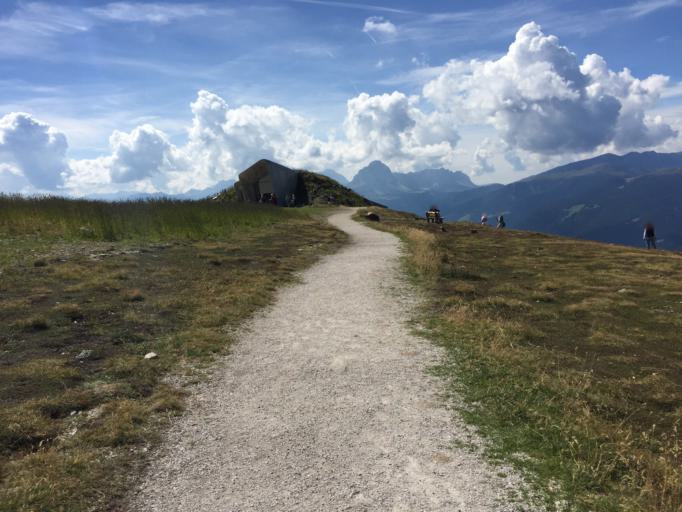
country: IT
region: Trentino-Alto Adige
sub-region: Bolzano
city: Riscone
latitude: 46.7381
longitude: 11.9554
